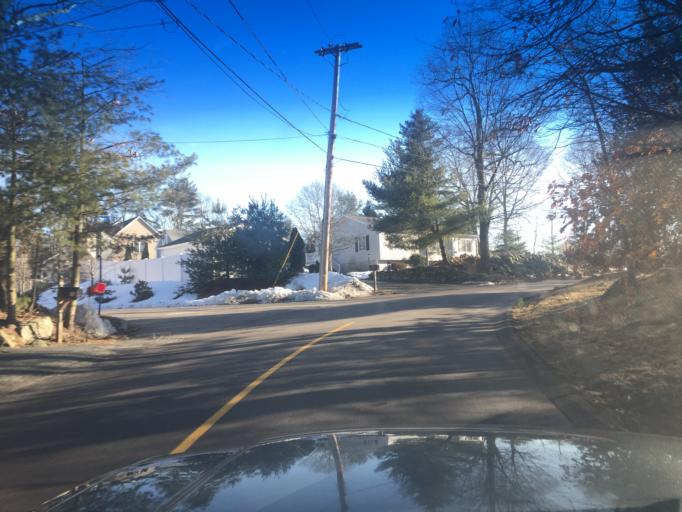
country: US
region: Massachusetts
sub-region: Norfolk County
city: Medway
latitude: 42.1440
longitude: -71.4531
